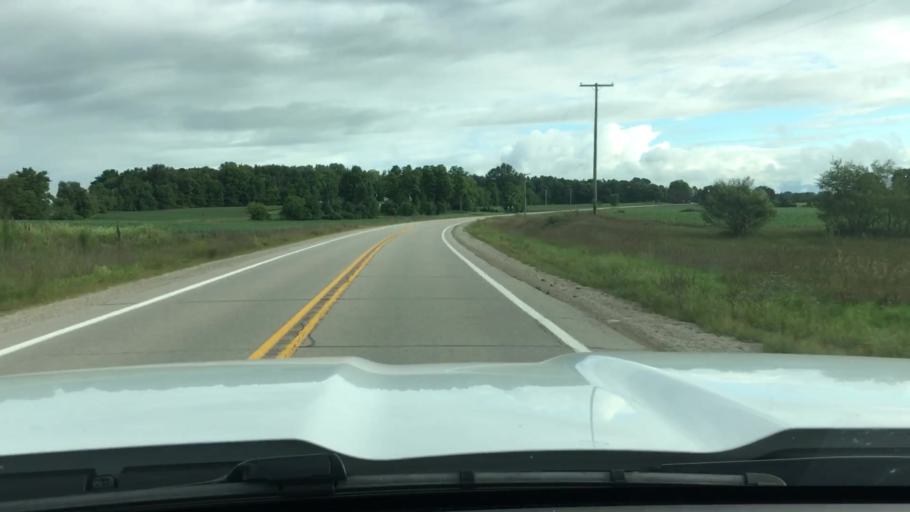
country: US
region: Michigan
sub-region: Tuscola County
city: Caro
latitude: 43.5323
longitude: -83.3447
